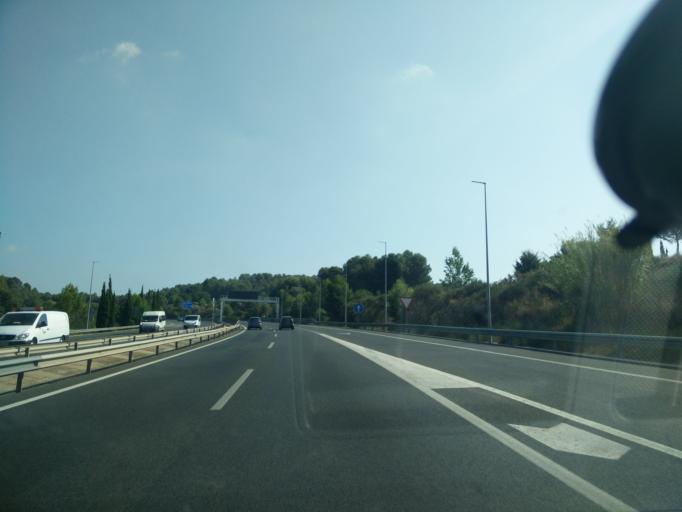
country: ES
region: Catalonia
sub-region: Provincia de Barcelona
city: Rubi
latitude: 41.5001
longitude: 2.0500
